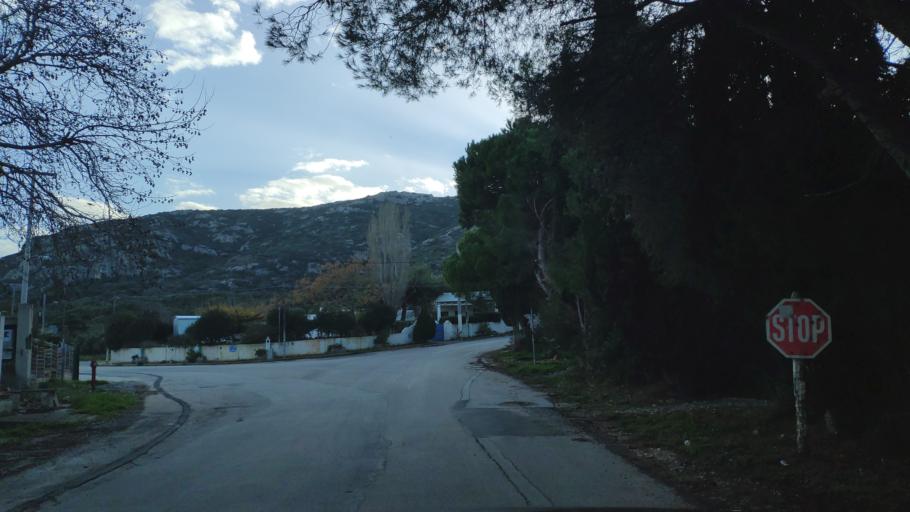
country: GR
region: Attica
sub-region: Nomarchia Anatolikis Attikis
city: Limin Mesoyaias
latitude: 37.9194
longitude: 24.0124
